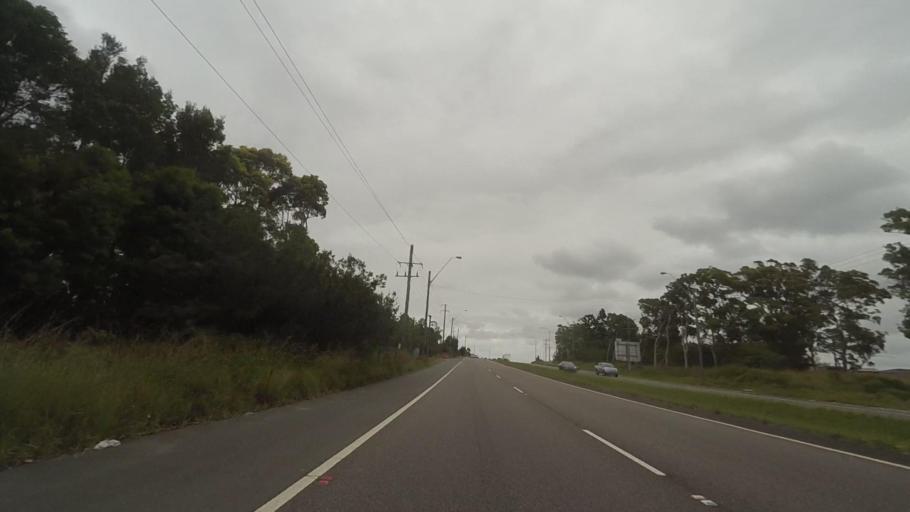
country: AU
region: New South Wales
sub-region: Wyong Shire
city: Buff Point
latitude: -33.2016
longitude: 151.5214
